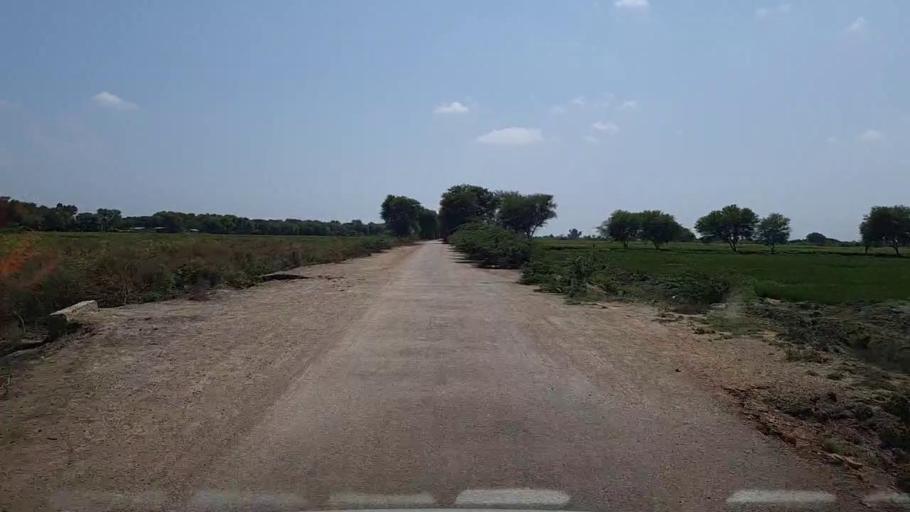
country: PK
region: Sindh
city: Kario
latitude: 24.8278
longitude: 68.7029
